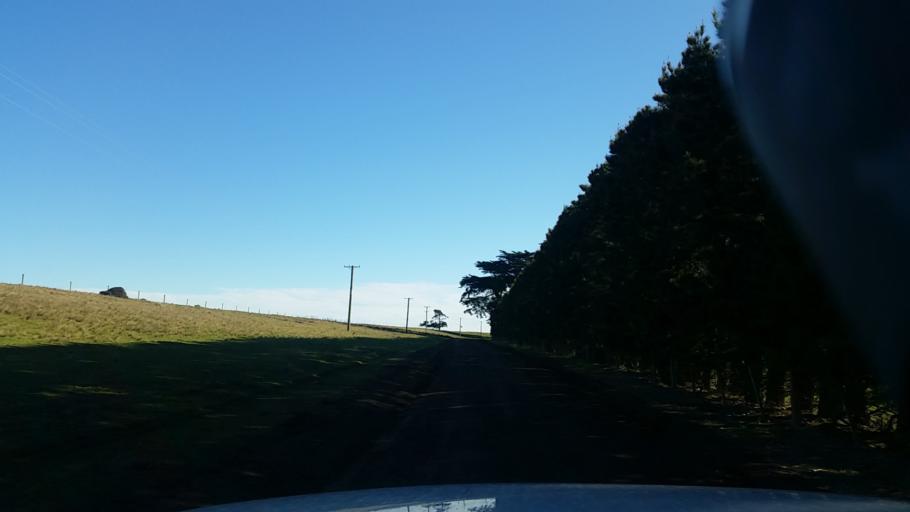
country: NZ
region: Canterbury
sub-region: Selwyn District
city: Lincoln
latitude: -43.8108
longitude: 172.6681
